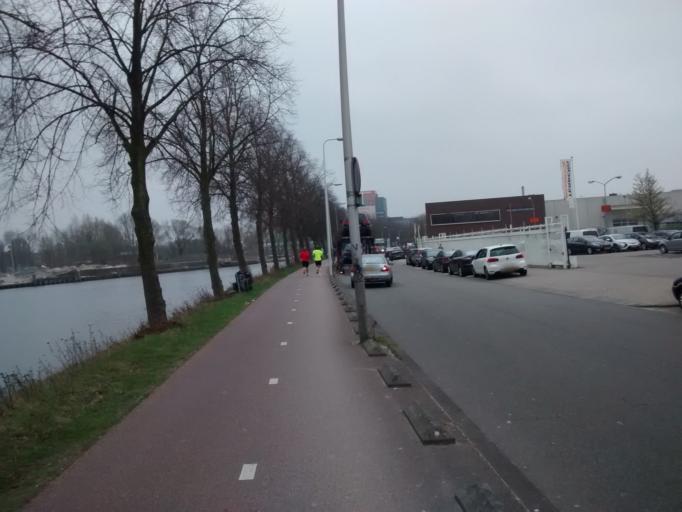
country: NL
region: Utrecht
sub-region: Gemeente Utrecht
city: Lunetten
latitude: 52.0634
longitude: 5.1125
